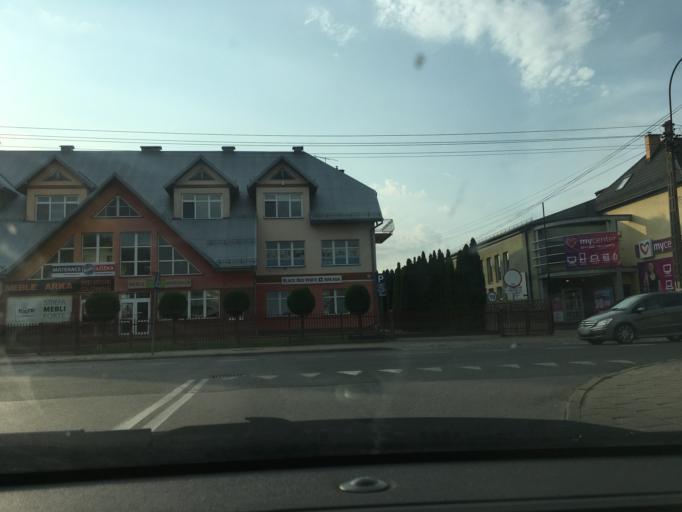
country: PL
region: Podlasie
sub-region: Powiat augustowski
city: Augustow
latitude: 53.8406
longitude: 22.9761
